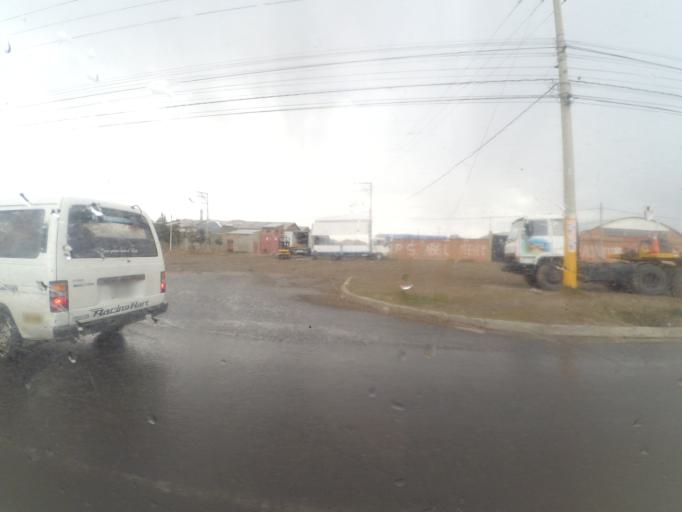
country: BO
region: La Paz
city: La Paz
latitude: -16.5540
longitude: -68.1800
